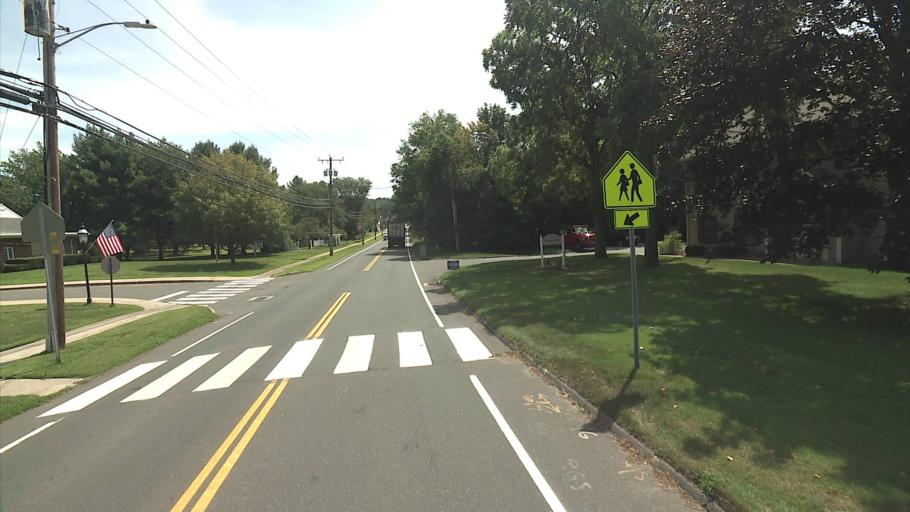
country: US
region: Connecticut
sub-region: Tolland County
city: Ellington
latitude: 41.9033
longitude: -72.4665
